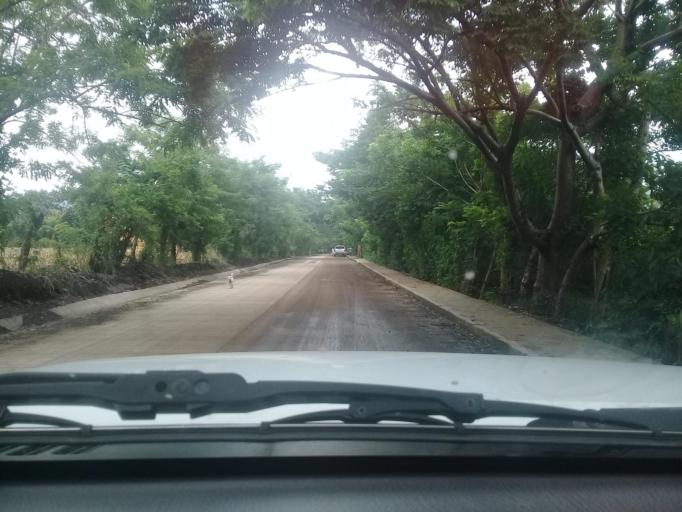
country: MX
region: Veracruz
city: Comoapan
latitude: 18.4125
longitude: -95.1806
